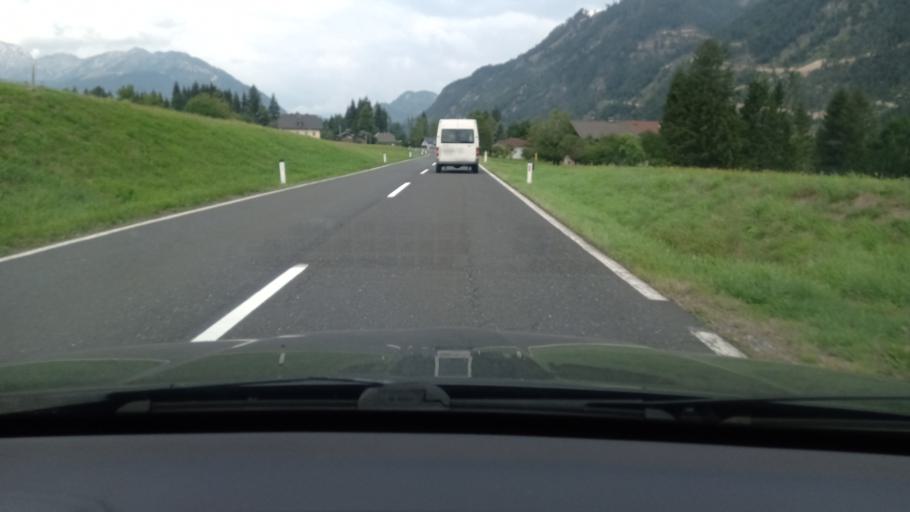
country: AT
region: Carinthia
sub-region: Politischer Bezirk Hermagor
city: Hermagor
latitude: 46.6645
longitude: 13.3063
